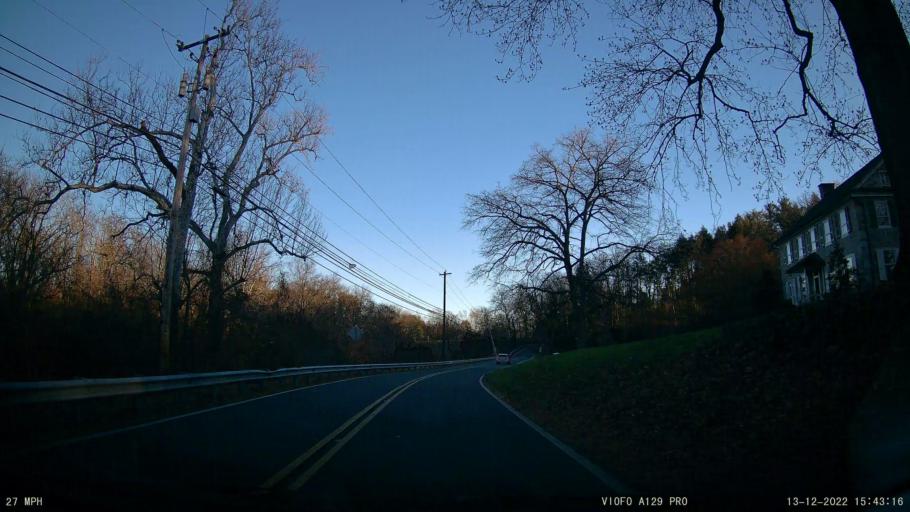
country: US
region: Pennsylvania
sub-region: Berks County
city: Spring Ridge
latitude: 40.3635
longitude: -75.9742
